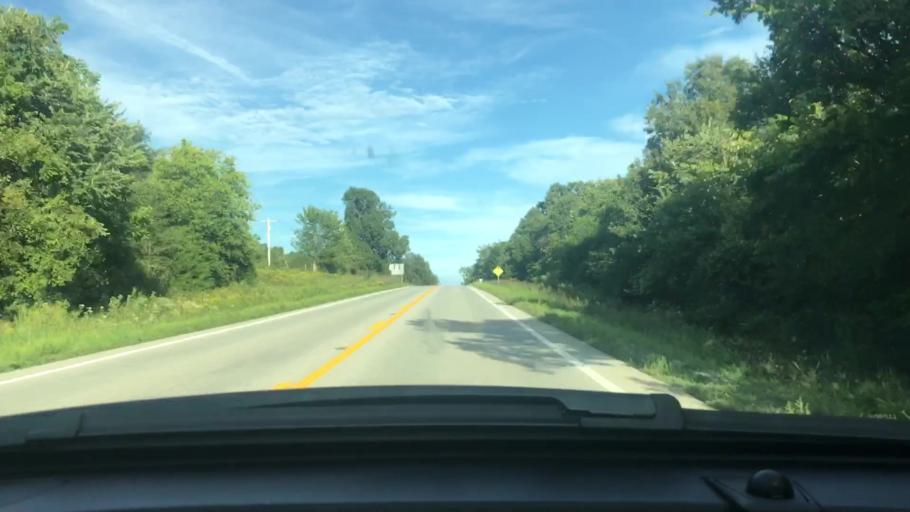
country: US
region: Arkansas
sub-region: Sharp County
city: Cherokee Village
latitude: 36.2744
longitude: -91.3438
